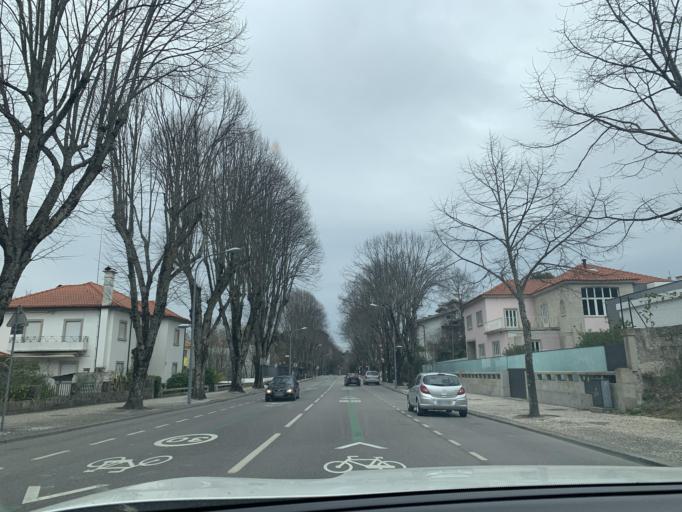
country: PT
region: Viseu
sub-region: Viseu
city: Viseu
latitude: 40.6527
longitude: -7.9166
